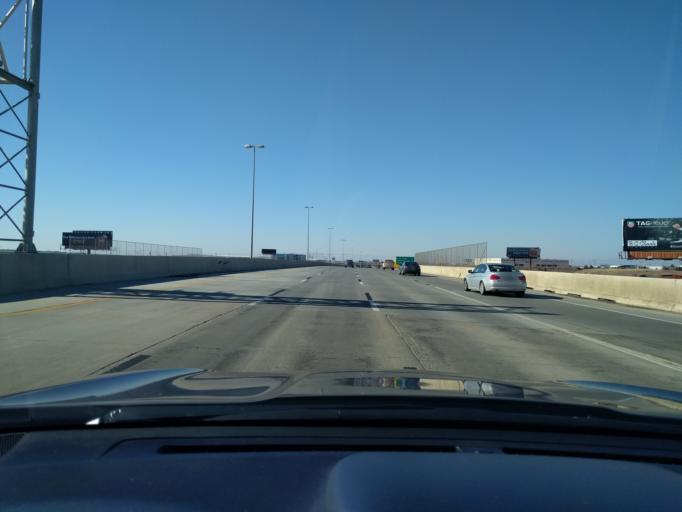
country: US
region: Oklahoma
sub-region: Oklahoma County
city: The Village
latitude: 35.5998
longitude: -97.5075
